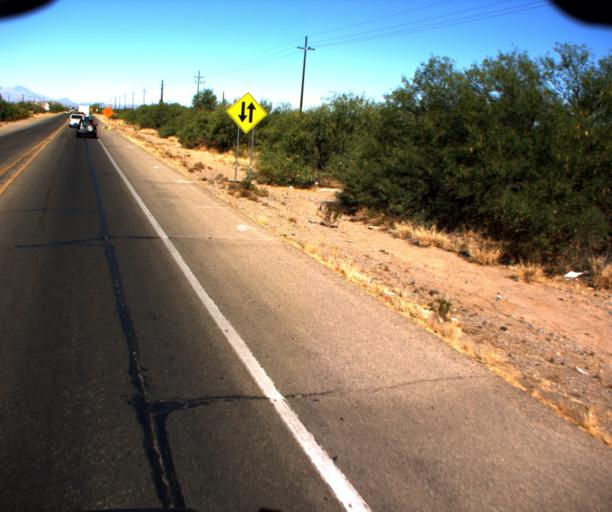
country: US
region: Arizona
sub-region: Pima County
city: Tucson Estates
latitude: 32.1698
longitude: -111.0772
